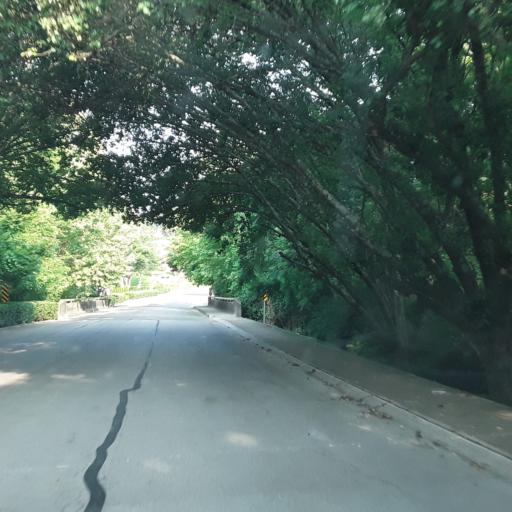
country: US
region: Tennessee
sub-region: Williamson County
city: Brentwood
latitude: 36.0553
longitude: -86.7436
